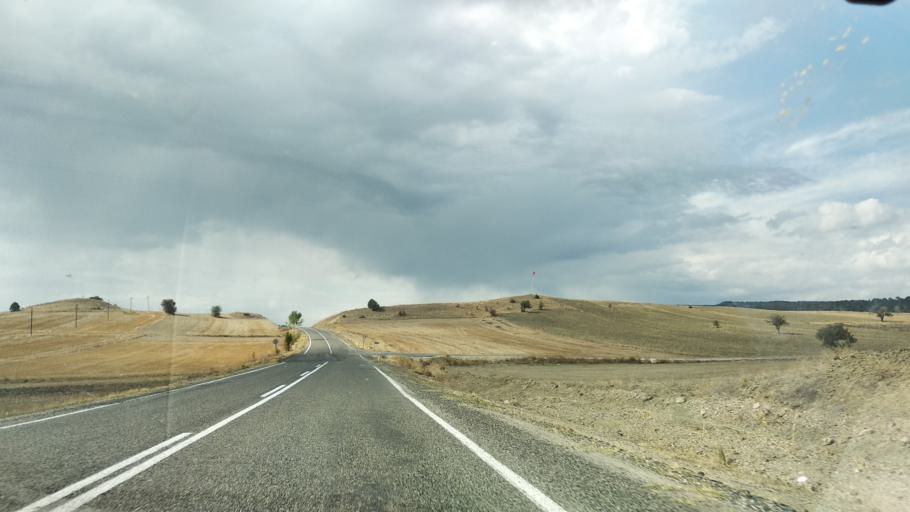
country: TR
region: Bolu
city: Seben
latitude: 40.3690
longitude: 31.5045
